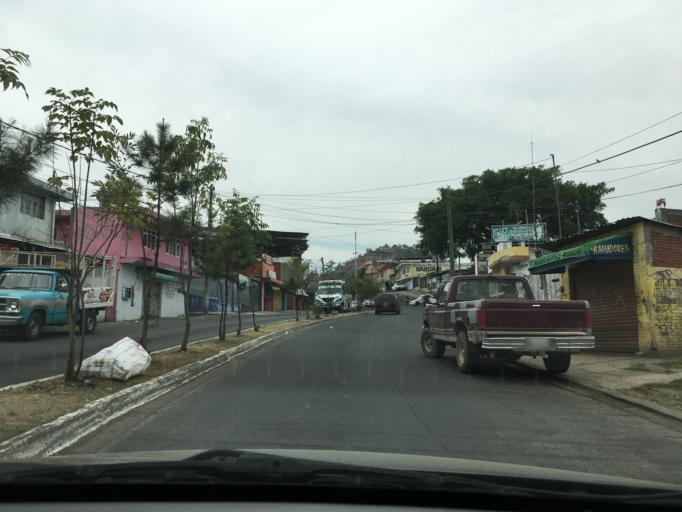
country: MX
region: Michoacan
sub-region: Uruapan
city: Uruapan
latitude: 19.4029
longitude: -102.0670
